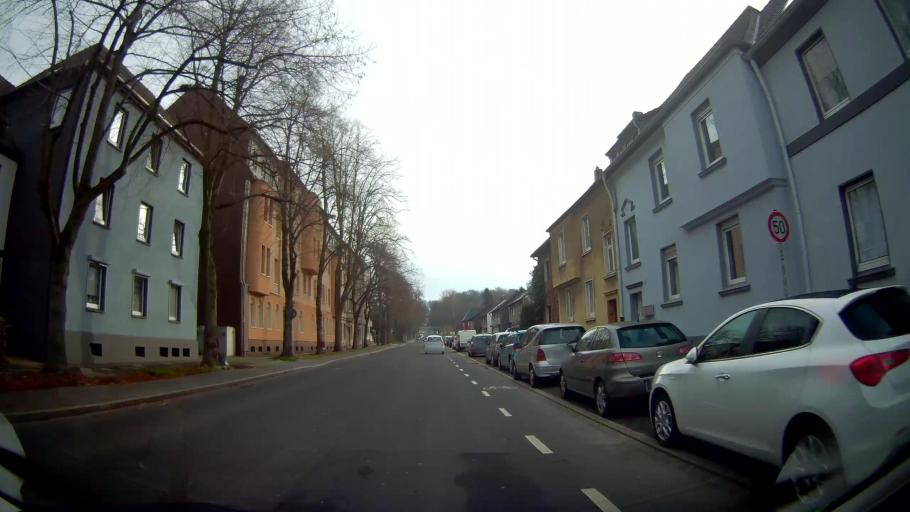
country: DE
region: North Rhine-Westphalia
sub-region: Regierungsbezirk Arnsberg
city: Herne
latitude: 51.5291
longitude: 7.2410
